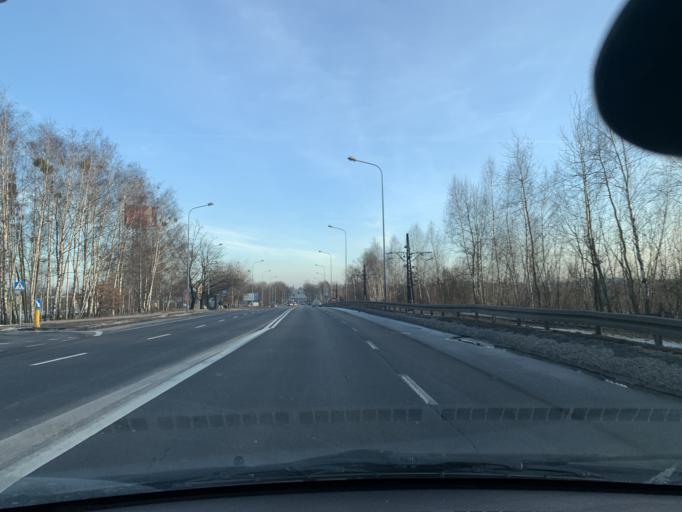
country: PL
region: Silesian Voivodeship
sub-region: Powiat tarnogorski
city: Radzionkow
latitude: 50.3797
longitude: 18.8868
